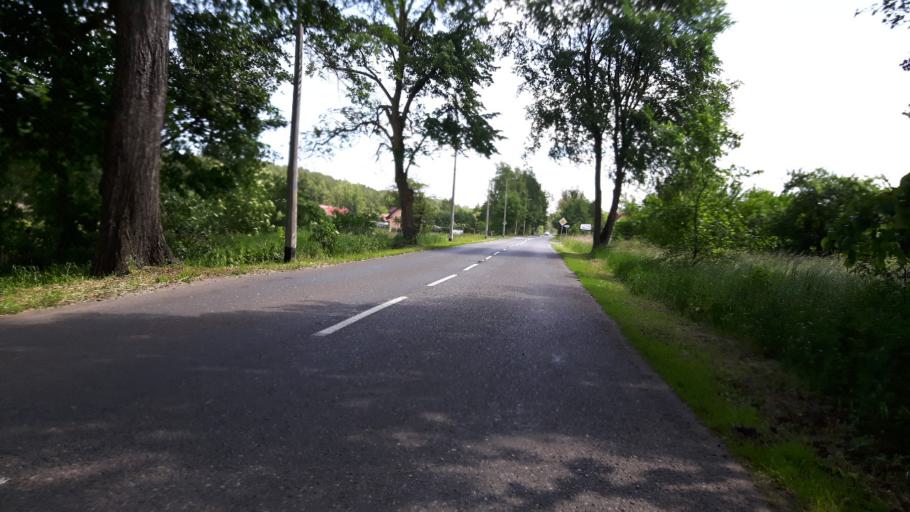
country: PL
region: Pomeranian Voivodeship
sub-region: Powiat gdanski
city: Cedry Wielkie
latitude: 54.3399
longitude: 18.8891
